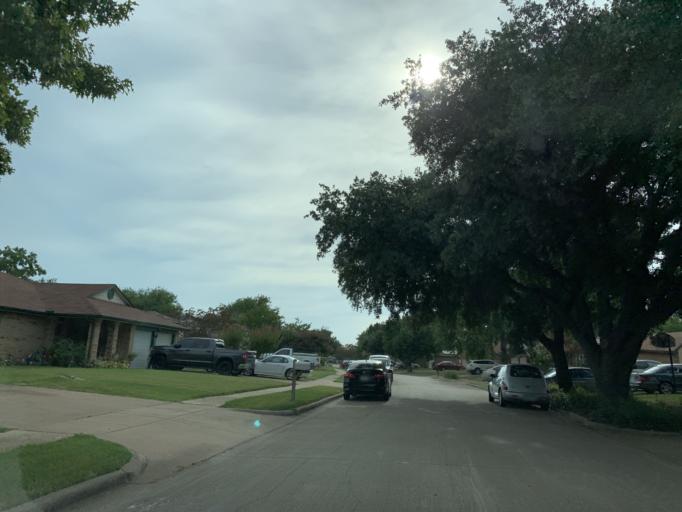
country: US
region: Texas
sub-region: Dallas County
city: Grand Prairie
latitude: 32.6664
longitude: -97.0445
